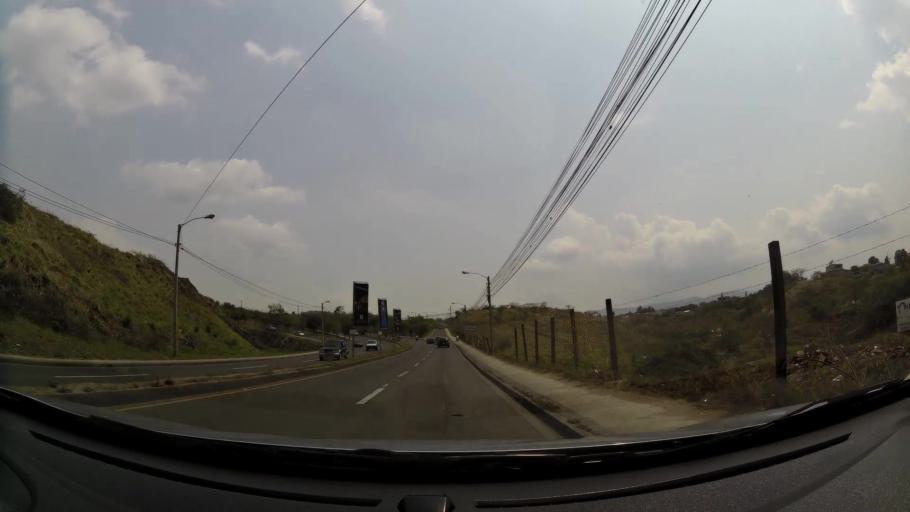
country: HN
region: Francisco Morazan
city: Yaguacire
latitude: 14.0475
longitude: -87.2237
